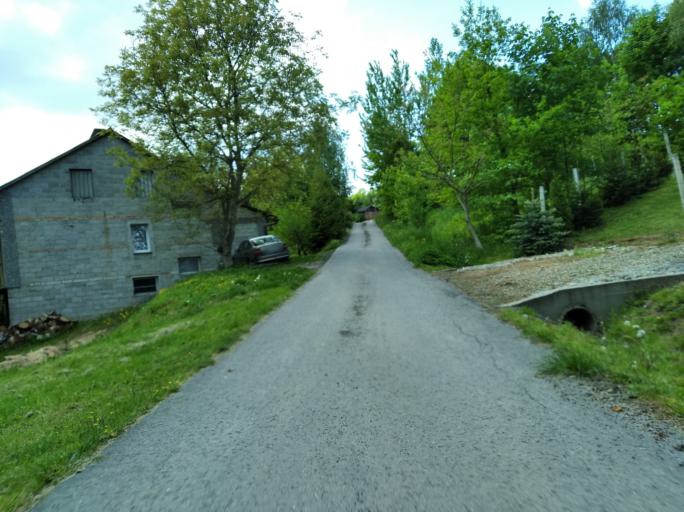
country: PL
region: Subcarpathian Voivodeship
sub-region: Powiat ropczycko-sedziszowski
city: Wielopole Skrzynskie
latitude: 49.9243
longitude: 21.6221
